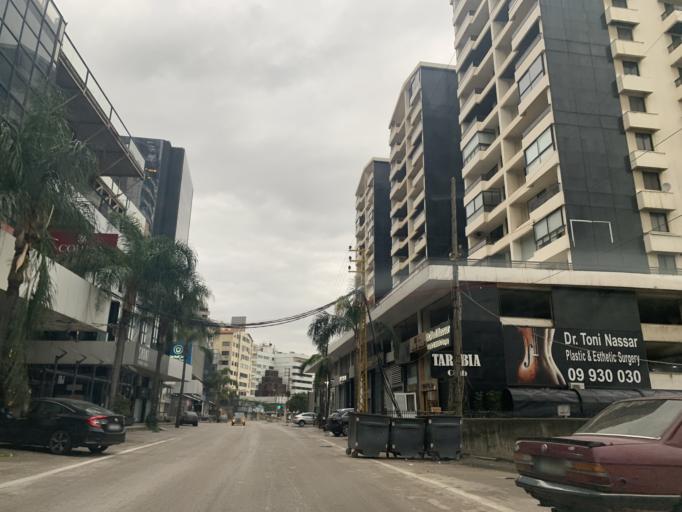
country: LB
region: Mont-Liban
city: Djounie
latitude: 33.9795
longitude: 35.6157
